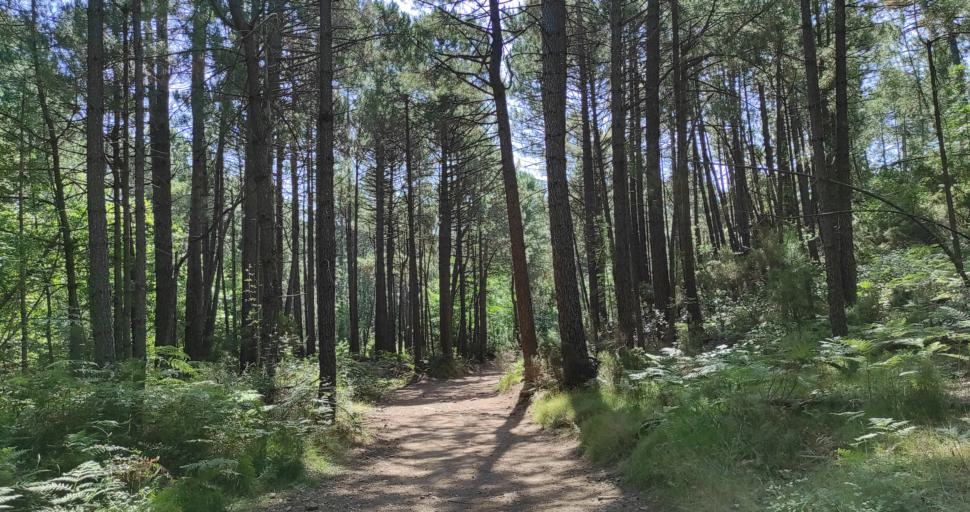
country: FR
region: Corsica
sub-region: Departement de la Corse-du-Sud
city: Zonza
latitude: 41.6835
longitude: 9.2083
